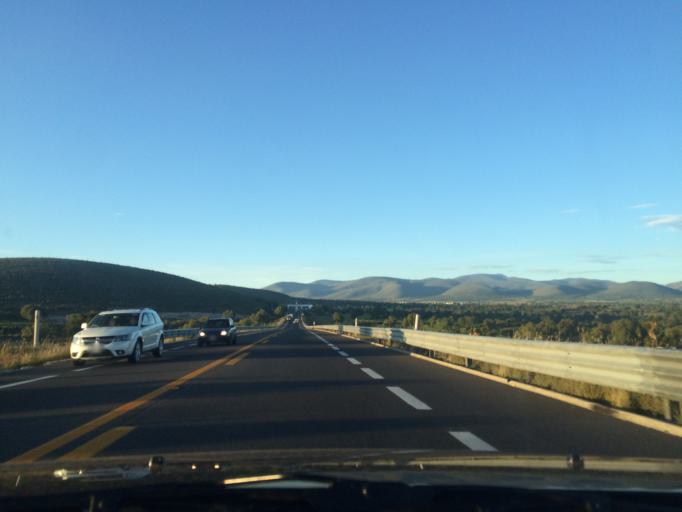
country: MX
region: Puebla
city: Cuacnopalan
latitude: 18.8023
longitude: -97.4900
